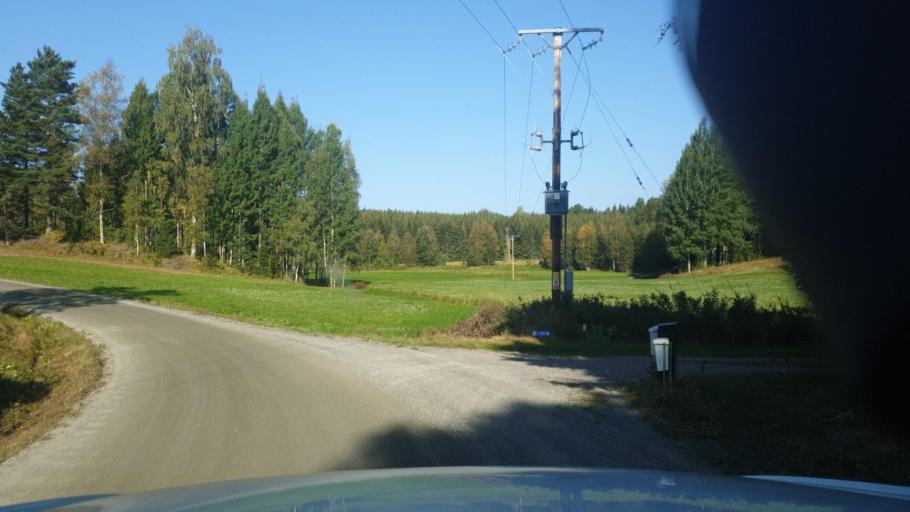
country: SE
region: Vaermland
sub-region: Sunne Kommun
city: Sunne
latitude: 59.6549
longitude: 13.0536
